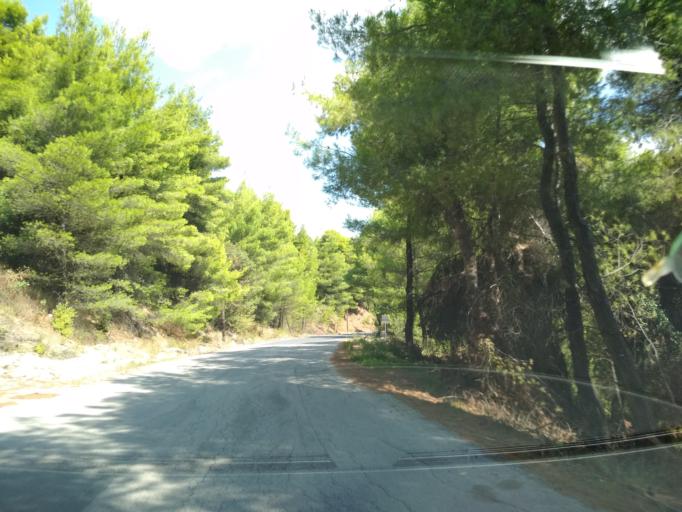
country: GR
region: Central Greece
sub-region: Nomos Evvoias
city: Roviai
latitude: 38.8184
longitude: 23.2772
